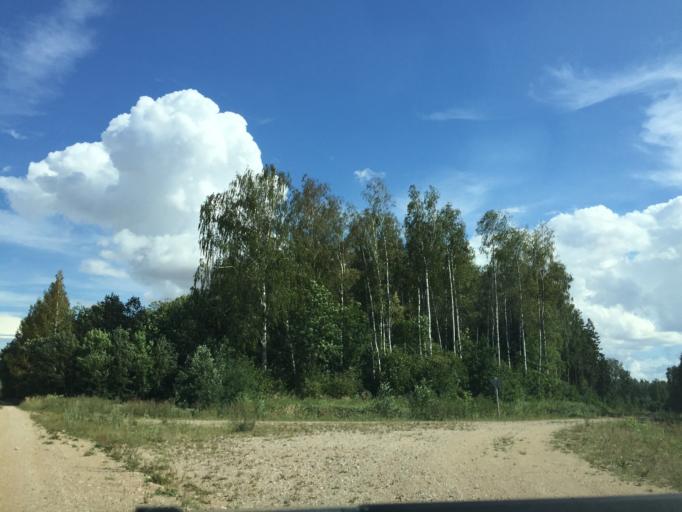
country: LT
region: Siauliu apskritis
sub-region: Joniskis
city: Joniskis
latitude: 56.3589
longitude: 23.5832
